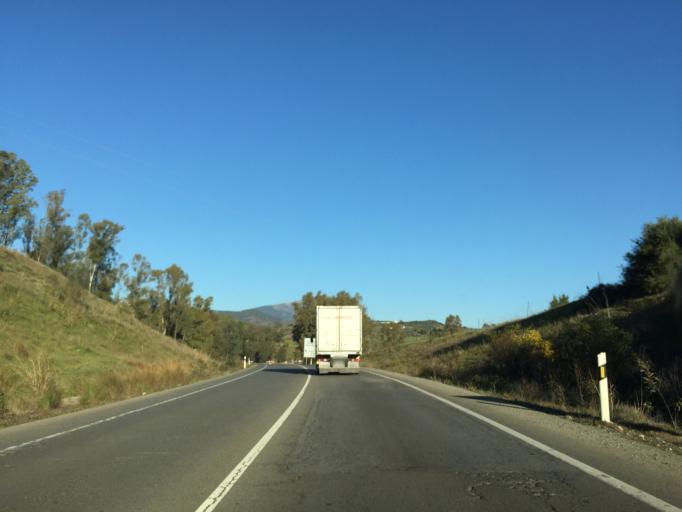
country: ES
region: Andalusia
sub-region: Provincia de Malaga
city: Pizarra
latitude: 36.7674
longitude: -4.7332
